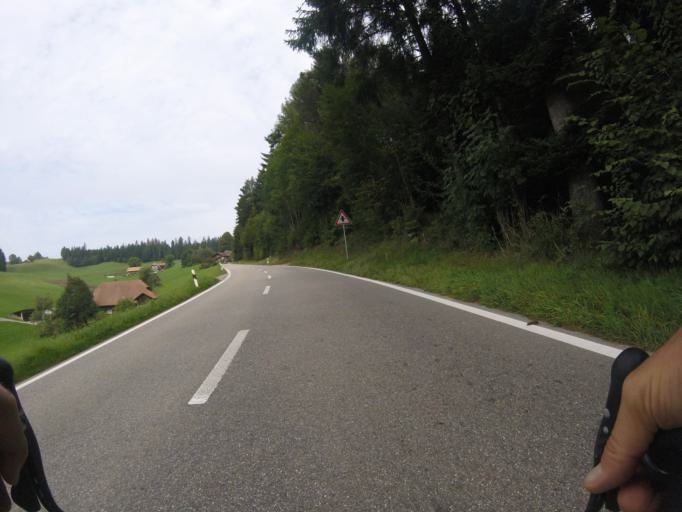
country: CH
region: Bern
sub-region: Bern-Mittelland District
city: Walkringen
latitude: 46.9459
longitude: 7.6503
